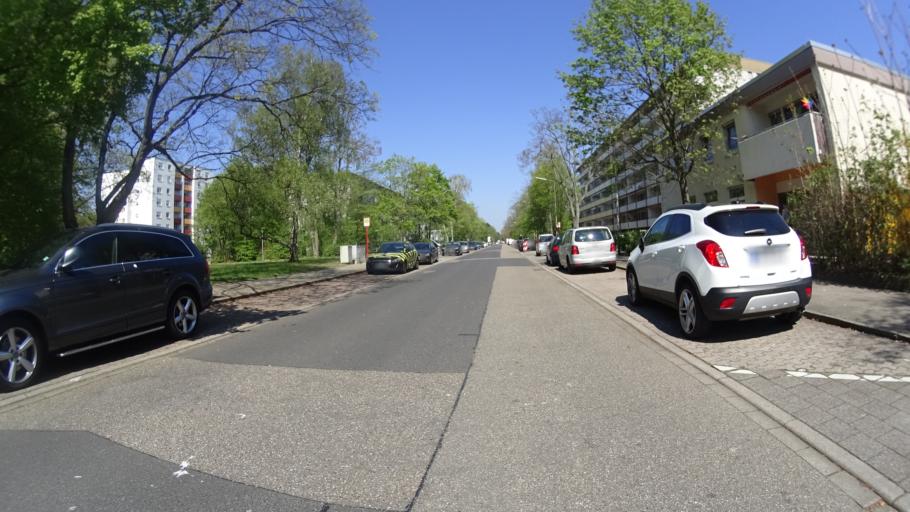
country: DE
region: Baden-Wuerttemberg
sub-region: Karlsruhe Region
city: Karlsruhe
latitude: 49.0258
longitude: 8.3745
